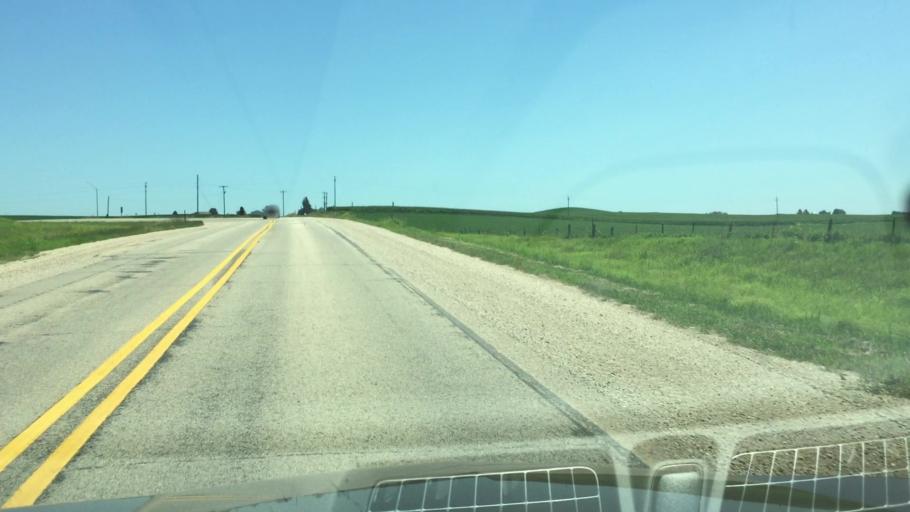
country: US
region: Iowa
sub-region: Cedar County
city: Mechanicsville
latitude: 41.9615
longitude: -91.1466
